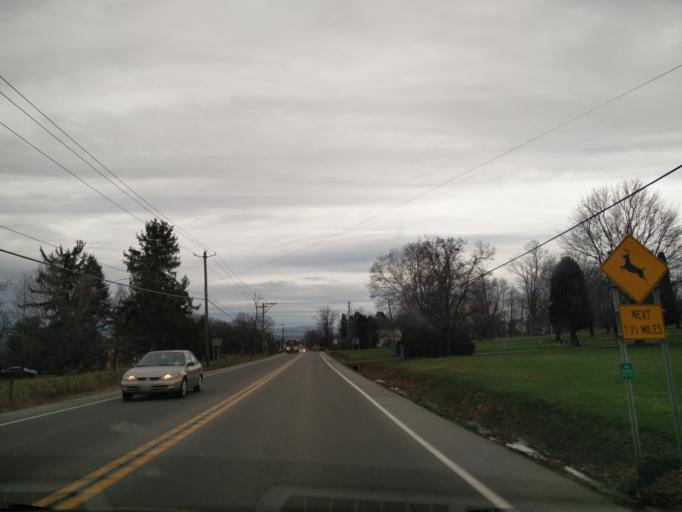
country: US
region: New York
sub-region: Tompkins County
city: Northwest Ithaca
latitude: 42.4693
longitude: -76.5439
